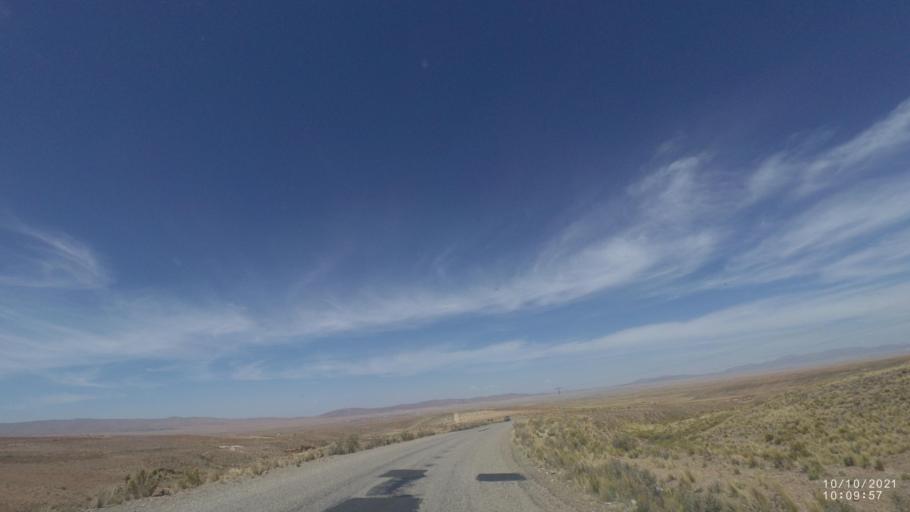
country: BO
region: La Paz
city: Eucaliptus
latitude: -17.4052
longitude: -67.4896
